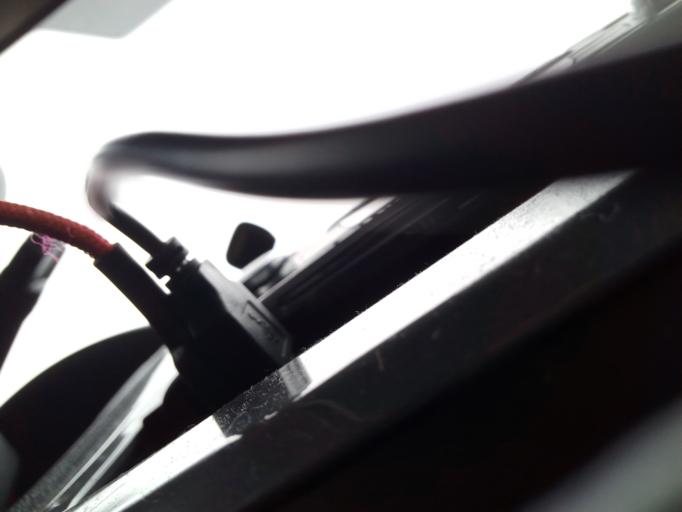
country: PL
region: Swietokrzyskie
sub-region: Powiat pinczowski
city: Dzialoszyce
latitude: 50.3909
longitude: 20.3297
